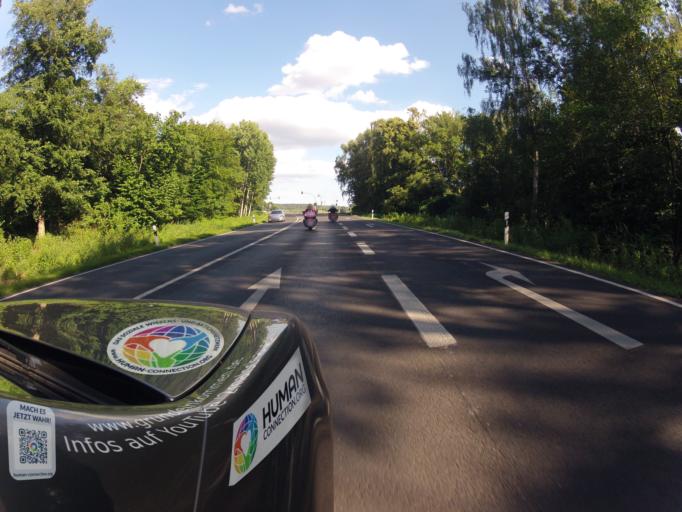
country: DE
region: Mecklenburg-Vorpommern
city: Seebad Bansin
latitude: 53.9836
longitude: 14.0768
